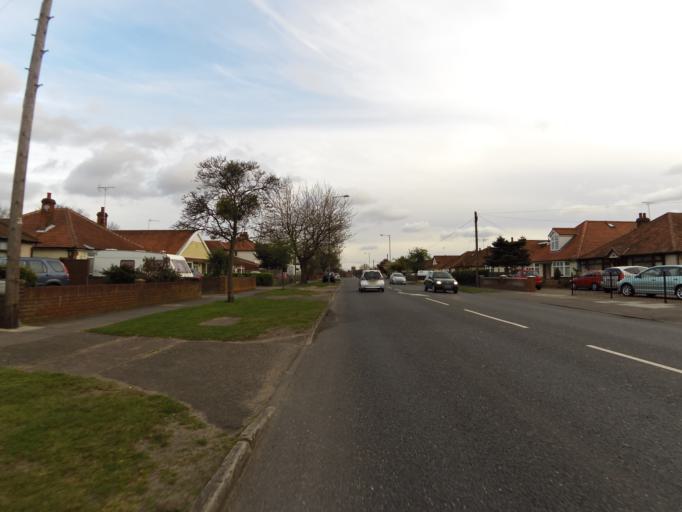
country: GB
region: England
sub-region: Suffolk
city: Kesgrave
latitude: 52.0482
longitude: 1.2007
